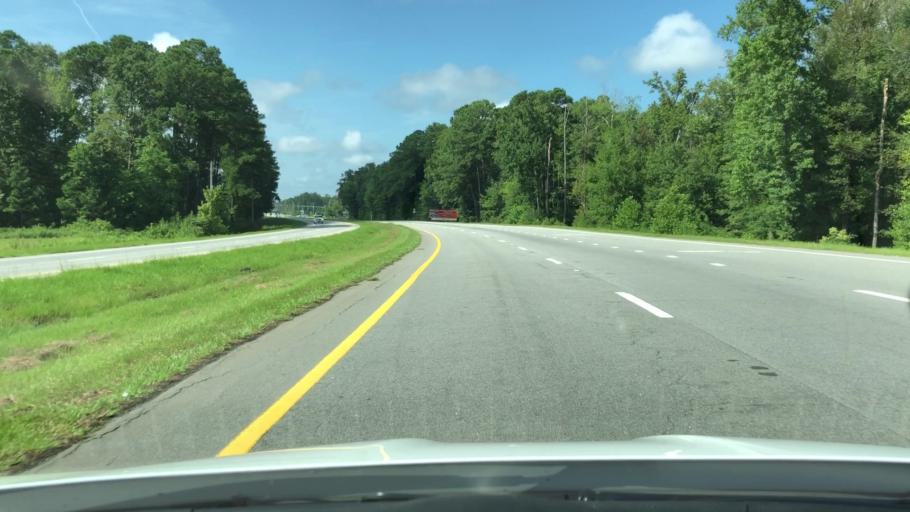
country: US
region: North Carolina
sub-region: Bertie County
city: Windsor
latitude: 36.0084
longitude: -76.9574
